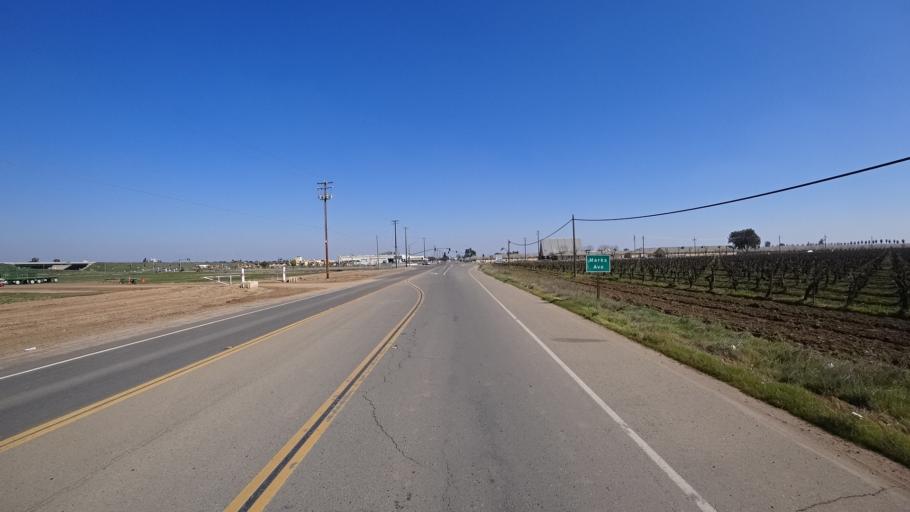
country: US
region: California
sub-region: Fresno County
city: West Park
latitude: 36.7356
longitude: -119.8464
